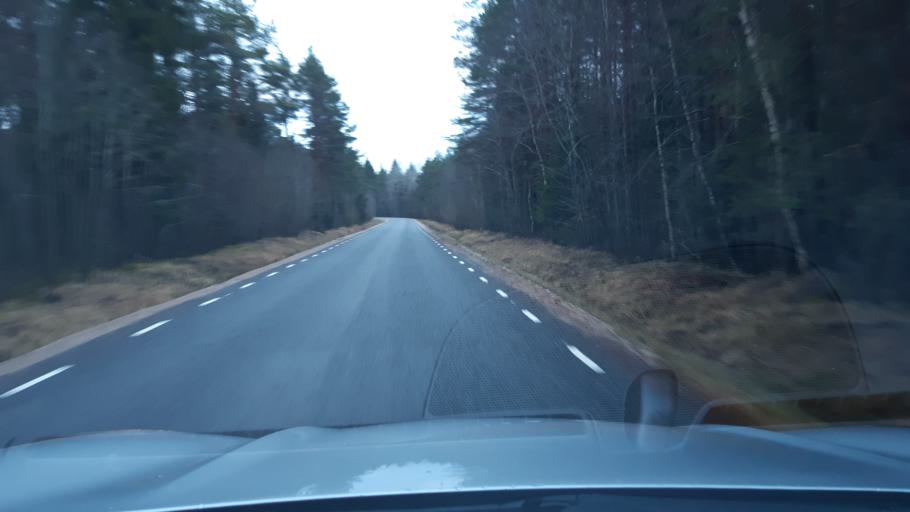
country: EE
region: Harju
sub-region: Saku vald
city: Saku
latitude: 59.1898
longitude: 24.6022
